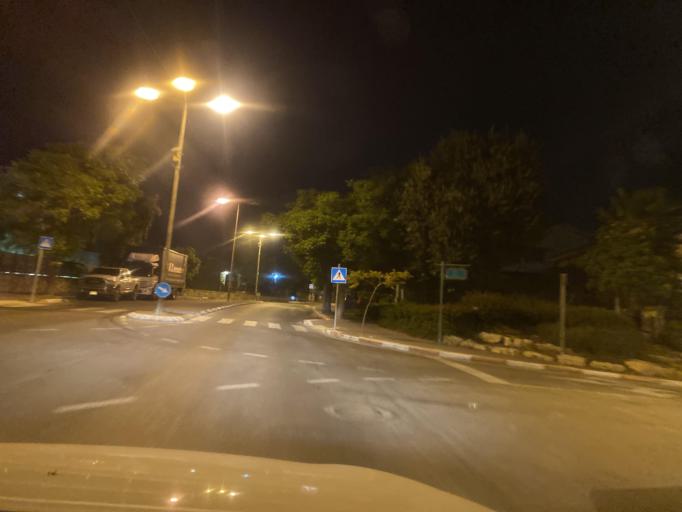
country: IL
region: Haifa
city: Daliyat el Karmil
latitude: 32.6392
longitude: 35.0847
